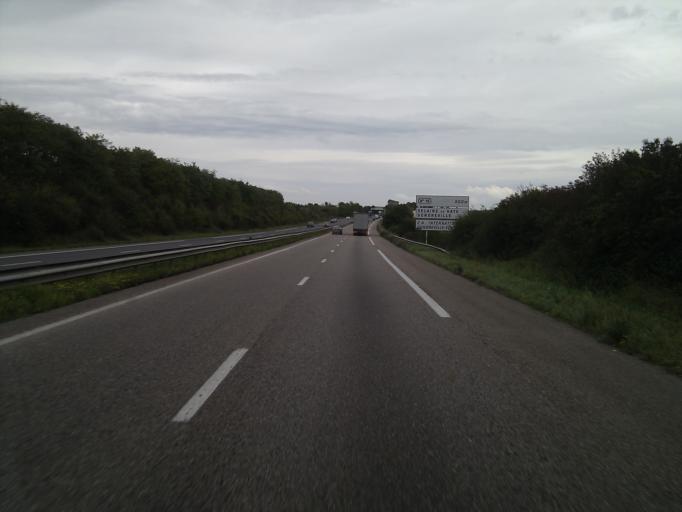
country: FR
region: Lorraine
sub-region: Departement de Meurthe-et-Moselle
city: Gondreville
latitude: 48.6877
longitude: 5.9632
